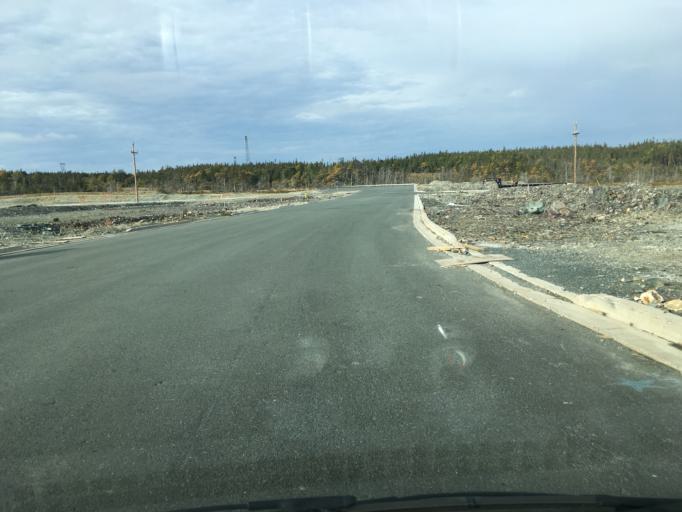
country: CA
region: Newfoundland and Labrador
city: Mount Pearl
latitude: 47.5571
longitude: -52.8031
